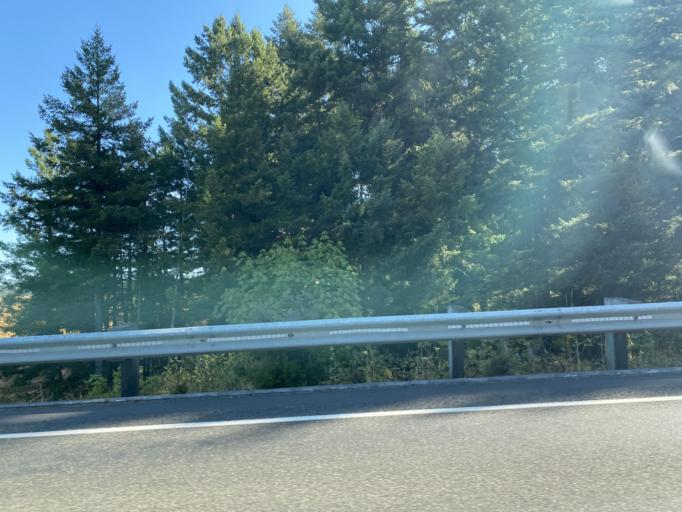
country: US
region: Washington
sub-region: Thurston County
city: Rainier
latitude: 46.9026
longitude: -122.7230
